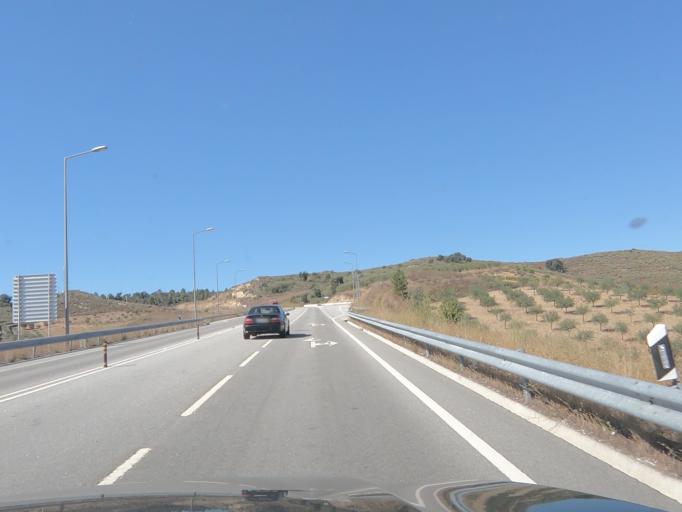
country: PT
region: Vila Real
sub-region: Valpacos
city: Valpacos
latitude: 41.5637
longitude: -7.2689
